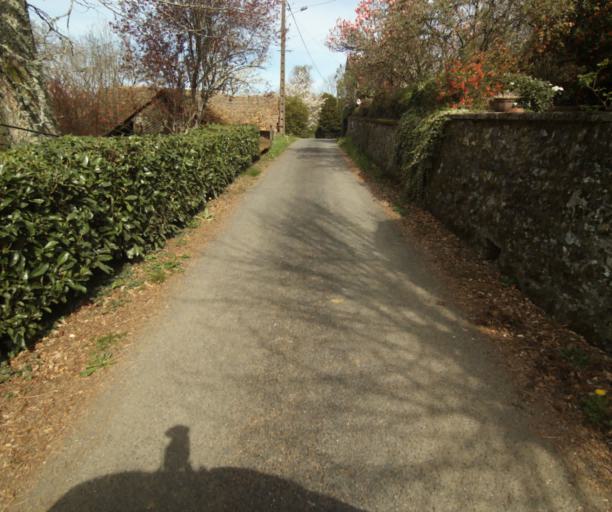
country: FR
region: Limousin
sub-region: Departement de la Correze
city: Naves
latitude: 45.3054
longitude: 1.7751
